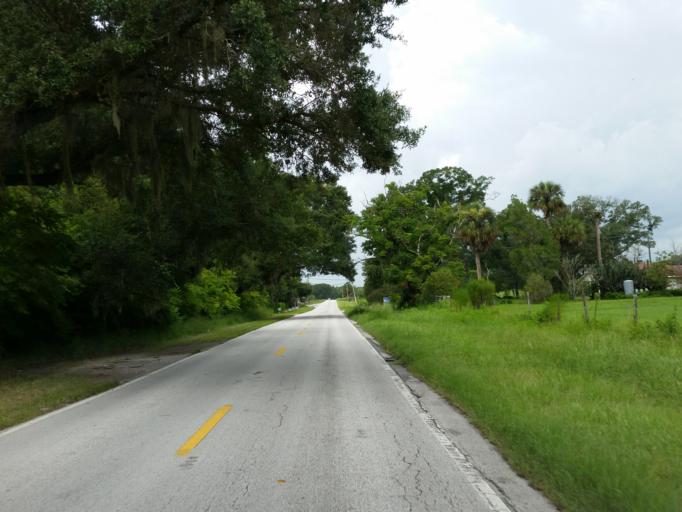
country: US
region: Florida
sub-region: Hillsborough County
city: Thonotosassa
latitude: 28.0471
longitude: -82.2545
